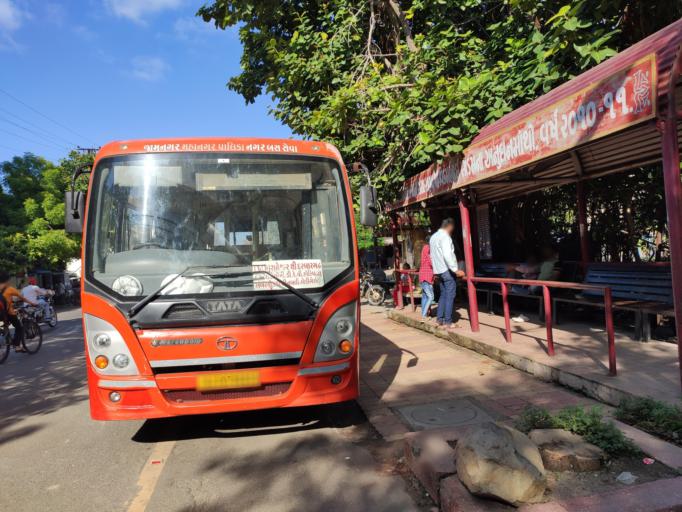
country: IN
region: Gujarat
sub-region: Jamnagar
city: Jamnagar
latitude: 22.4860
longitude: 70.0647
